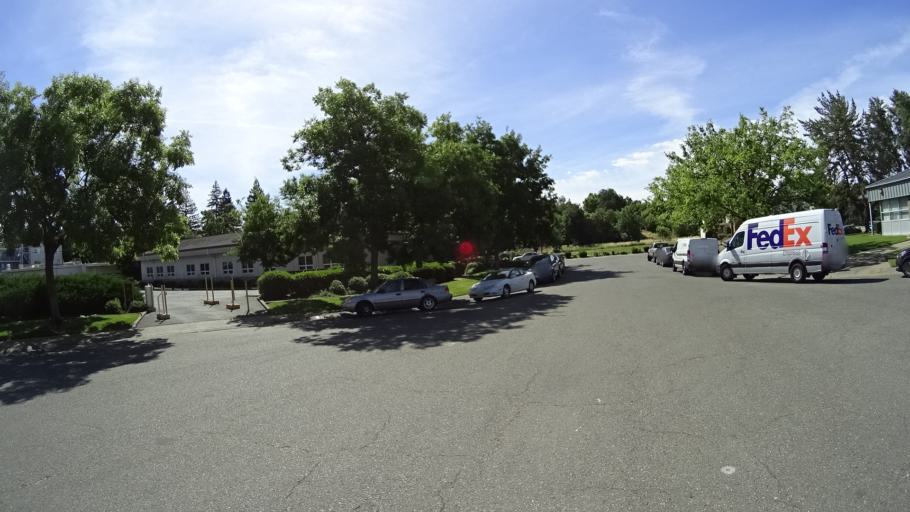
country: US
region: California
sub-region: Sacramento County
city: Arden-Arcade
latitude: 38.5665
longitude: -121.4309
